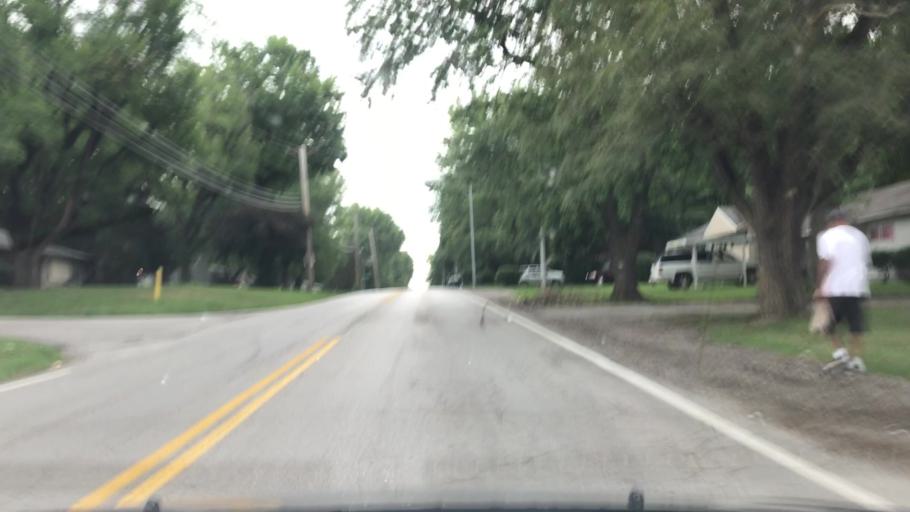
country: US
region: Missouri
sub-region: Jackson County
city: Grandview
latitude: 38.9304
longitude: -94.5037
